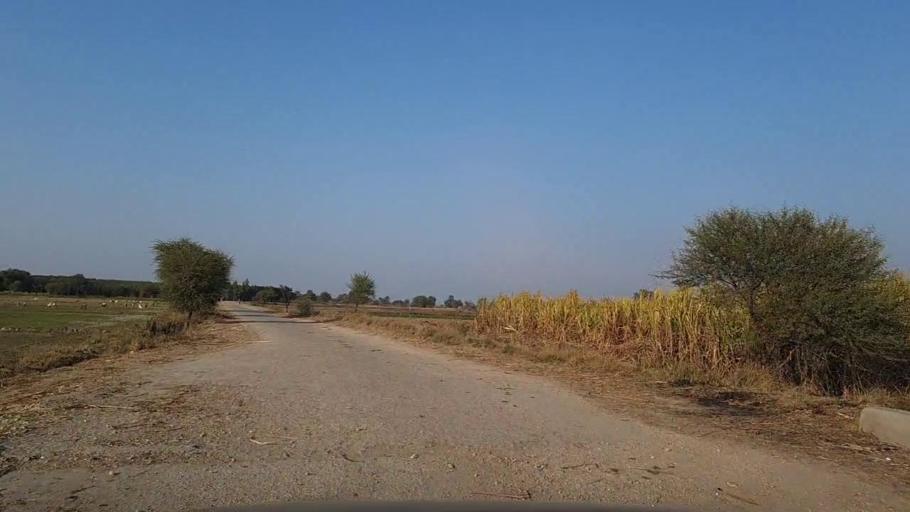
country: PK
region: Sindh
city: Tando Mittha Khan
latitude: 25.9382
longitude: 69.0712
